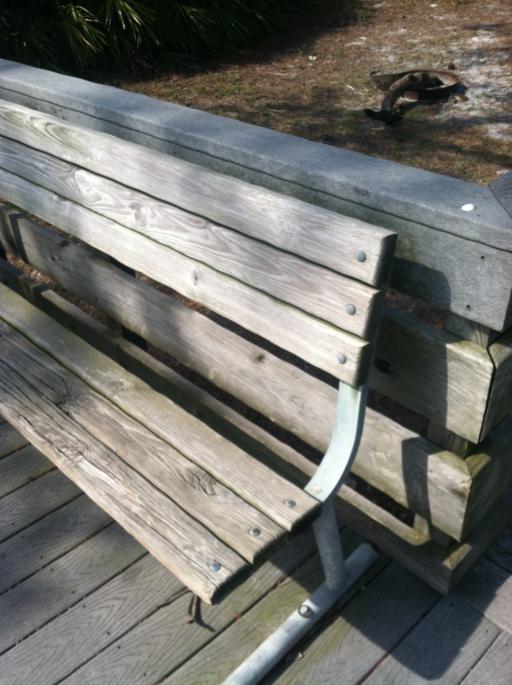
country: US
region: Florida
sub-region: Gulf County
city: Port Saint Joe
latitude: 29.7871
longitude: -85.4049
